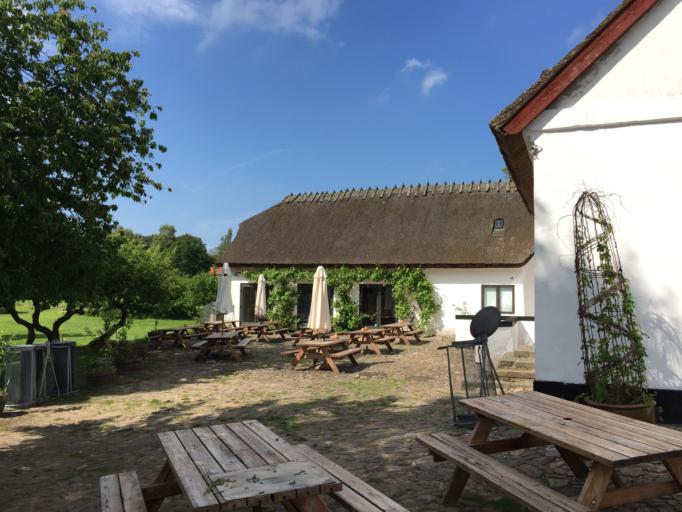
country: DK
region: Capital Region
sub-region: Hillerod Kommune
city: Nodebo
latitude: 56.0461
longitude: 12.3768
